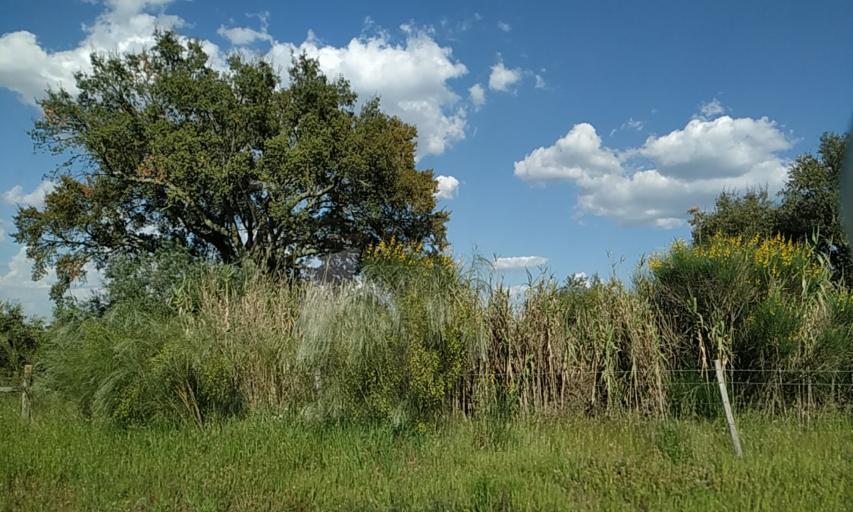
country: PT
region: Evora
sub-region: Estremoz
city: Estremoz
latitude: 38.8733
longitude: -7.5634
